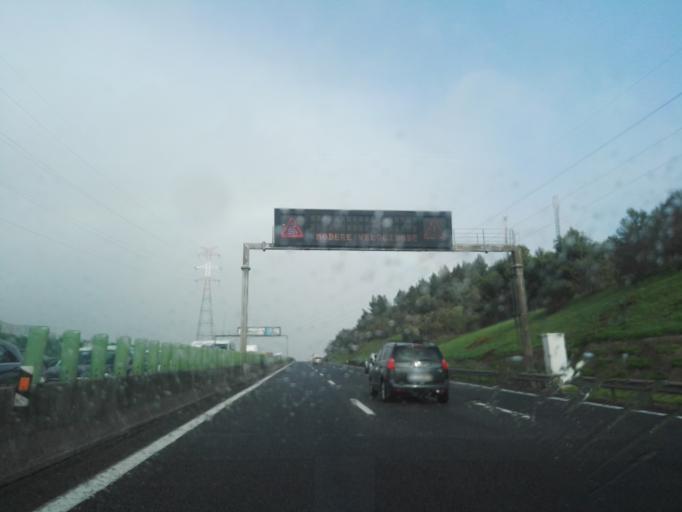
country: PT
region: Lisbon
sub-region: Vila Franca de Xira
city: Vialonga
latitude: 38.8747
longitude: -9.0667
